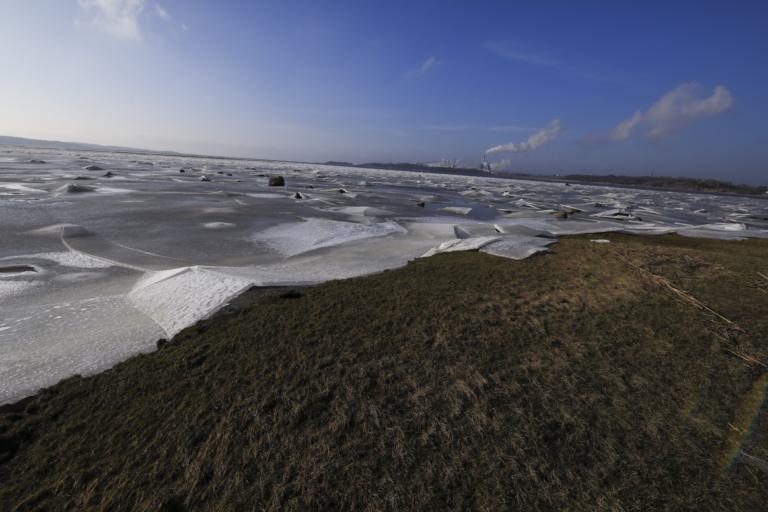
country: SE
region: Halland
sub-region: Kungsbacka Kommun
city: Frillesas
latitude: 57.2211
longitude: 12.2134
